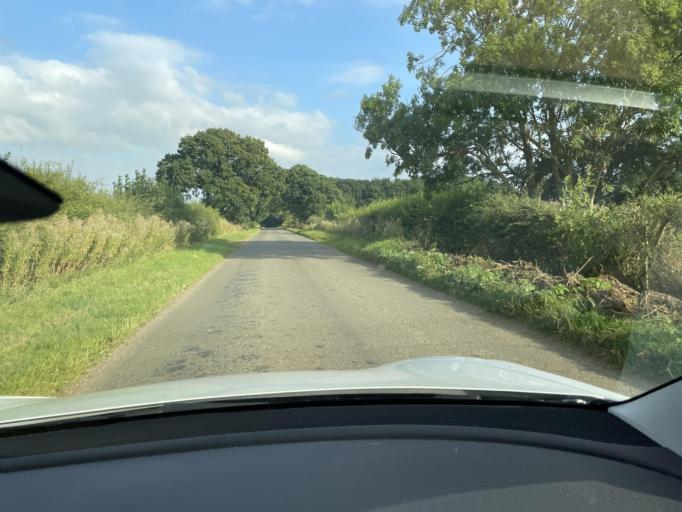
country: GB
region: England
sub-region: Leicestershire
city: Market Harborough
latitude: 52.4057
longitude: -1.0101
